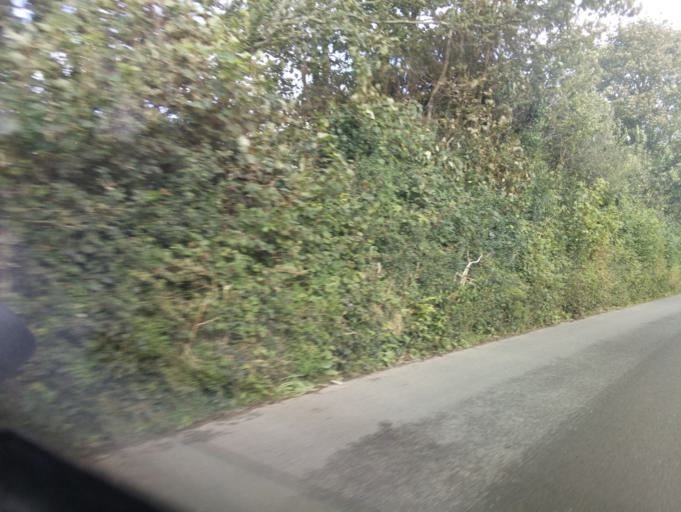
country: GB
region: England
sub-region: Devon
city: Ivybridge
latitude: 50.3527
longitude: -3.9273
